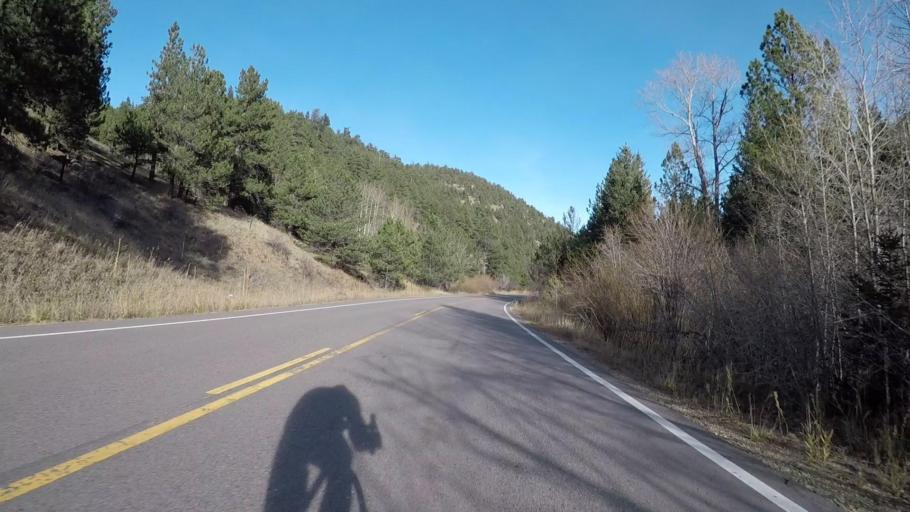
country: US
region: Colorado
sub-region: Boulder County
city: Nederland
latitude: 40.0627
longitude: -105.4830
